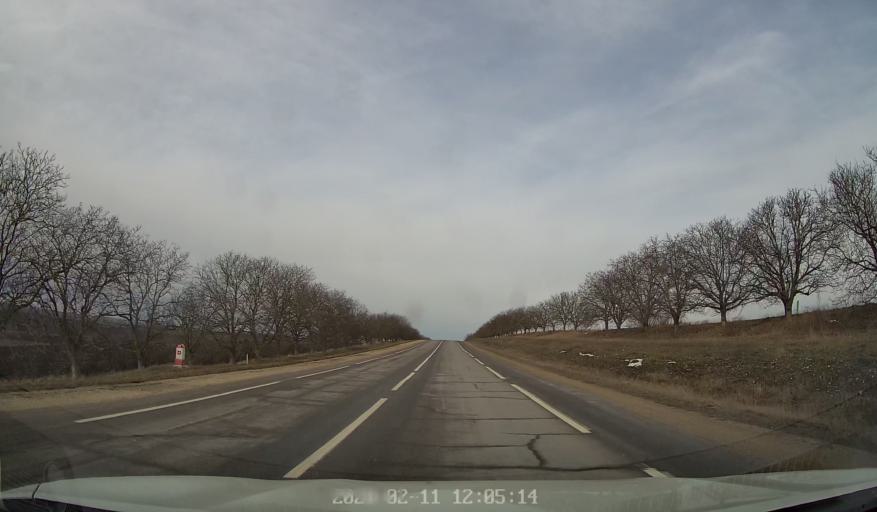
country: MD
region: Riscani
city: Riscani
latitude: 47.9790
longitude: 27.5845
